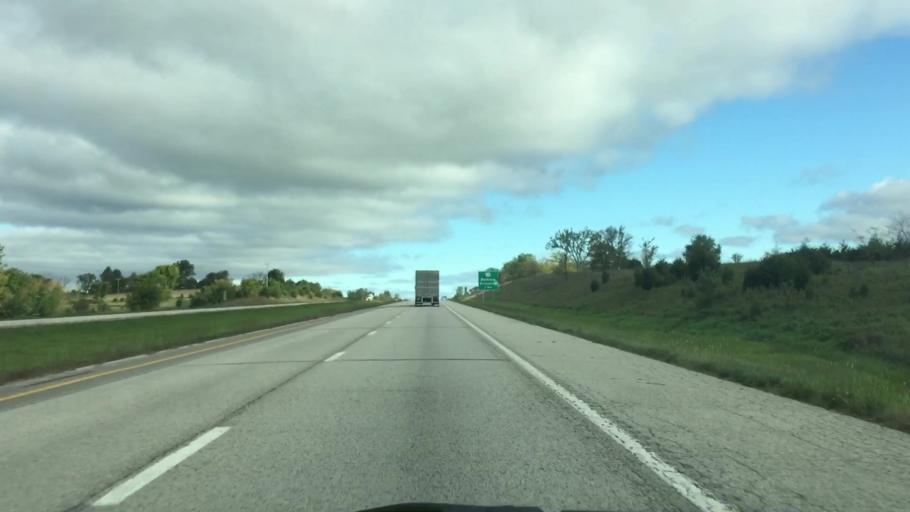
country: US
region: Missouri
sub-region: Harrison County
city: Bethany
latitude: 40.2434
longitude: -94.0127
